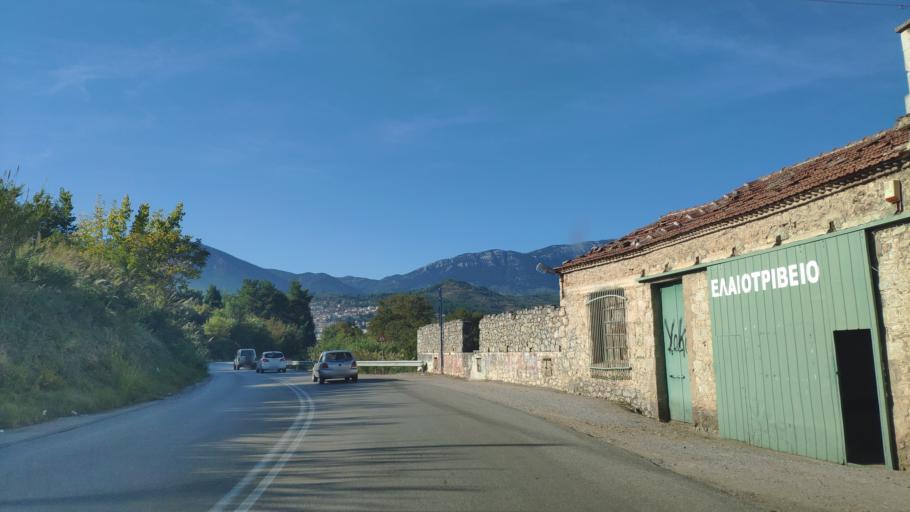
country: GR
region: Central Greece
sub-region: Nomos Voiotias
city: Livadeia
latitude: 38.4467
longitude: 22.8803
